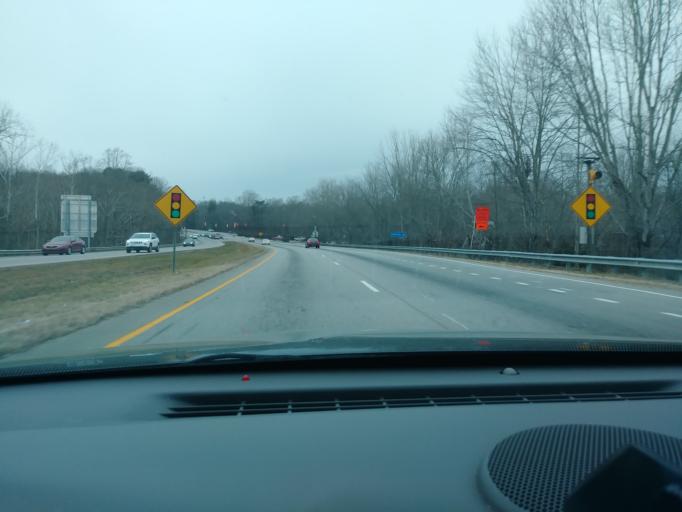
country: US
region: North Carolina
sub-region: Wilkes County
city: Wilkesboro
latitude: 36.1491
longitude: -81.1826
